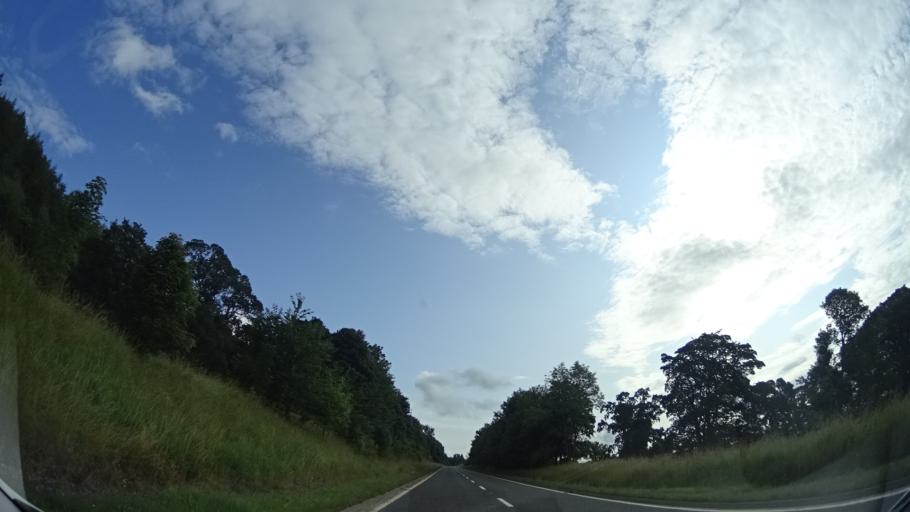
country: GB
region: Scotland
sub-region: Highland
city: Muir of Ord
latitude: 57.5611
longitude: -4.4933
